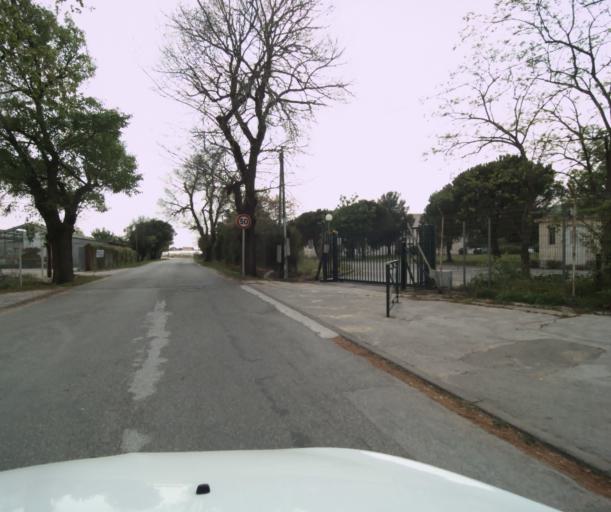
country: FR
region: Provence-Alpes-Cote d'Azur
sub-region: Departement du Var
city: Hyeres
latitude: 43.0948
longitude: 6.1366
